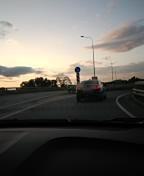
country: RU
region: Moskovskaya
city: Ostrovtsy
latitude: 55.5671
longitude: 38.0386
